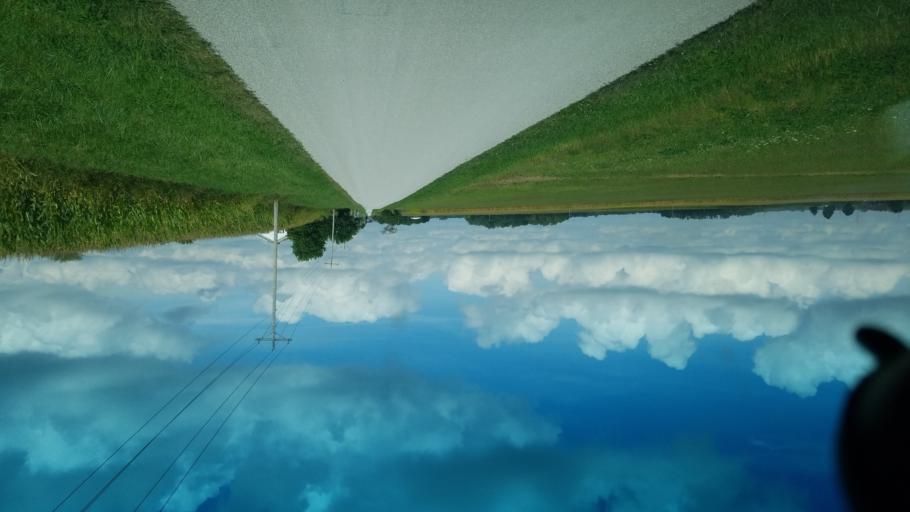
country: US
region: Ohio
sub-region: Seneca County
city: Tiffin
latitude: 40.9735
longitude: -83.1128
